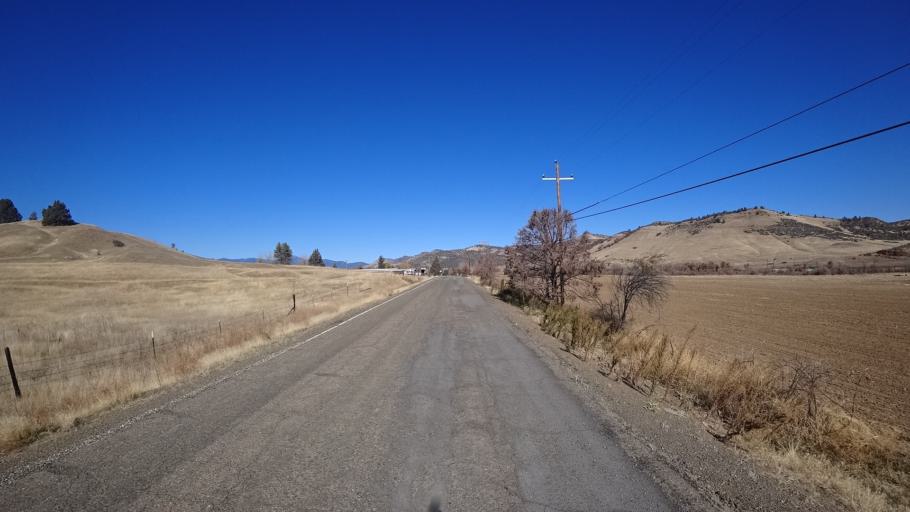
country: US
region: California
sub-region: Siskiyou County
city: Montague
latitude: 41.8960
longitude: -122.5508
